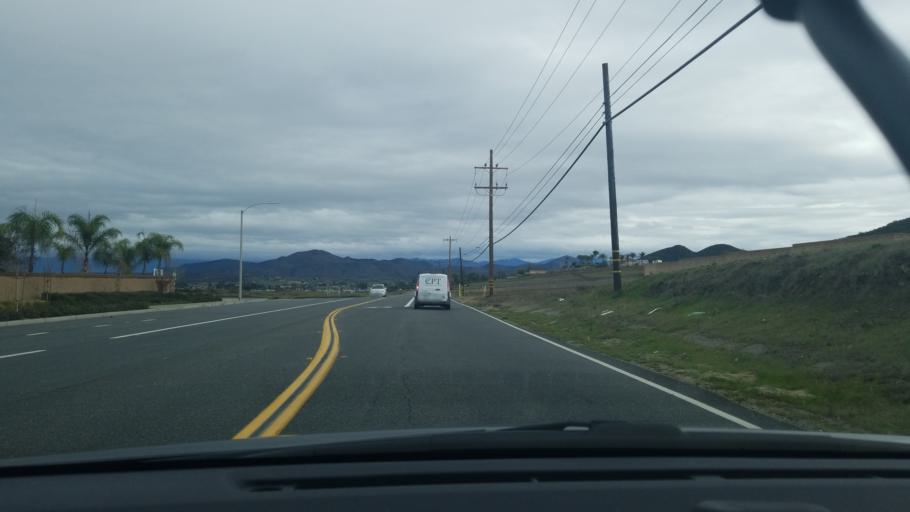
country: US
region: California
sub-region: Riverside County
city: Winchester
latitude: 33.6415
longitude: -117.1332
